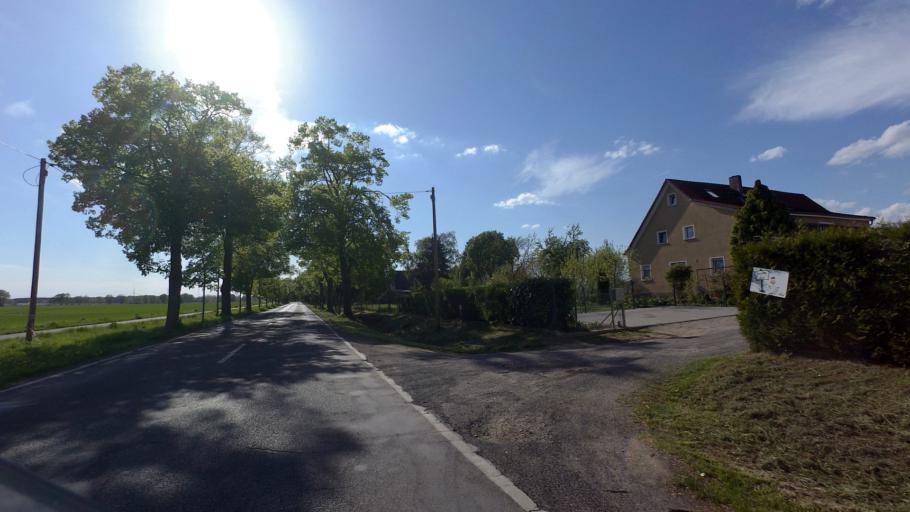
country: DE
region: Brandenburg
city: Liebenwalde
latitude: 52.7786
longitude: 13.3577
